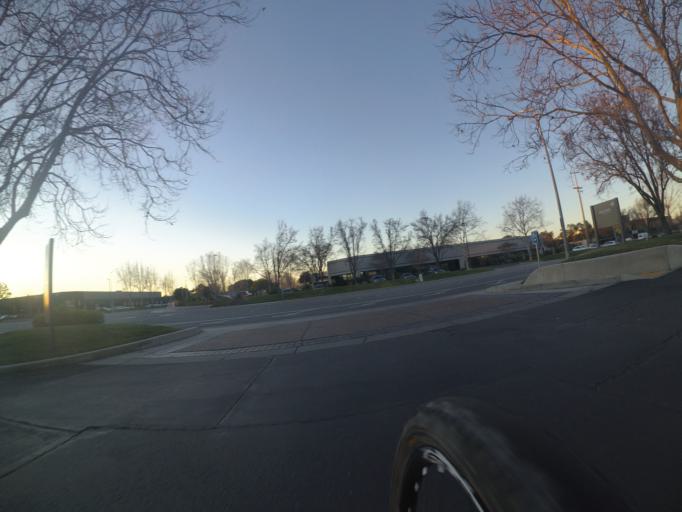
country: US
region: California
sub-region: Santa Clara County
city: Milpitas
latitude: 37.4749
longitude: -121.9392
